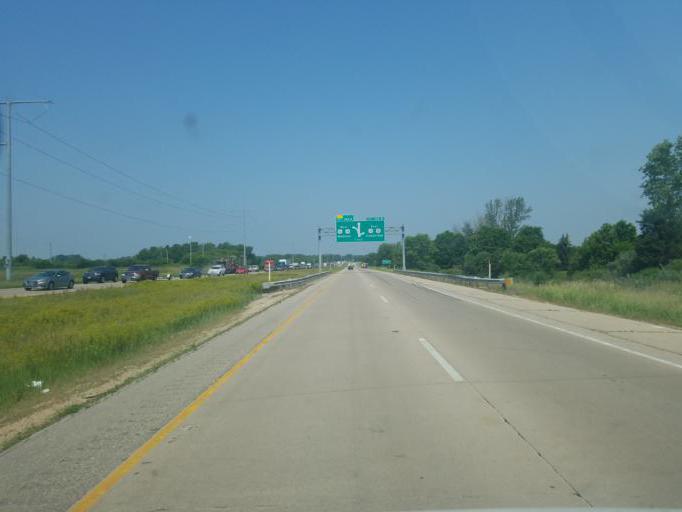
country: US
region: Wisconsin
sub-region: Dane County
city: McFarland
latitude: 43.0318
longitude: -89.2618
